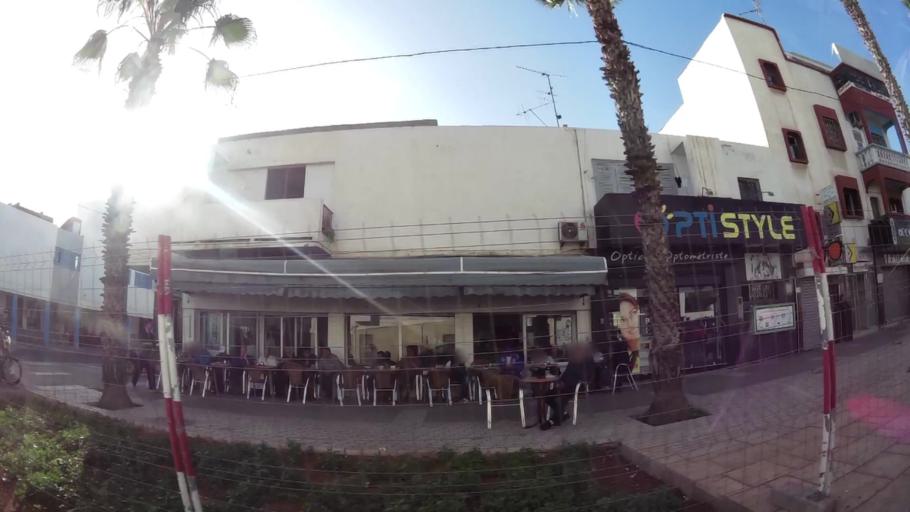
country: MA
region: Souss-Massa-Draa
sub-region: Agadir-Ida-ou-Tnan
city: Agadir
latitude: 30.4235
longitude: -9.5920
